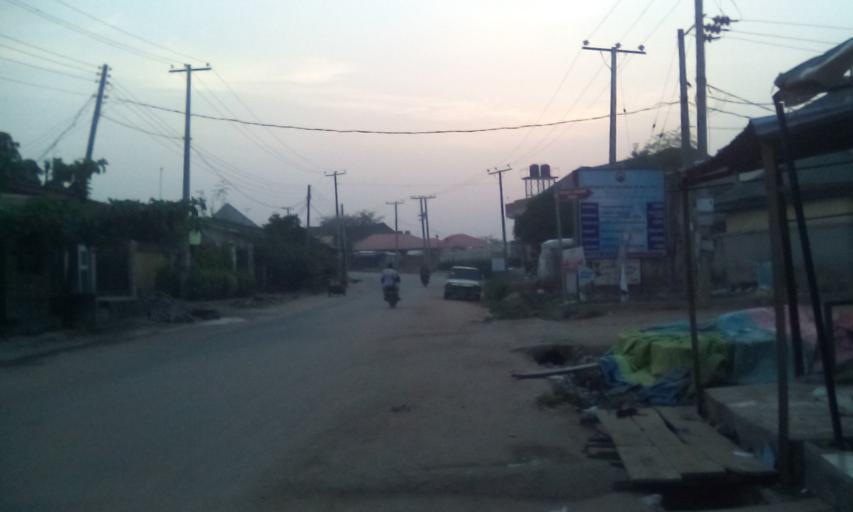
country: NG
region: Abuja Federal Capital Territory
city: Abuja
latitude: 8.9837
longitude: 7.3550
